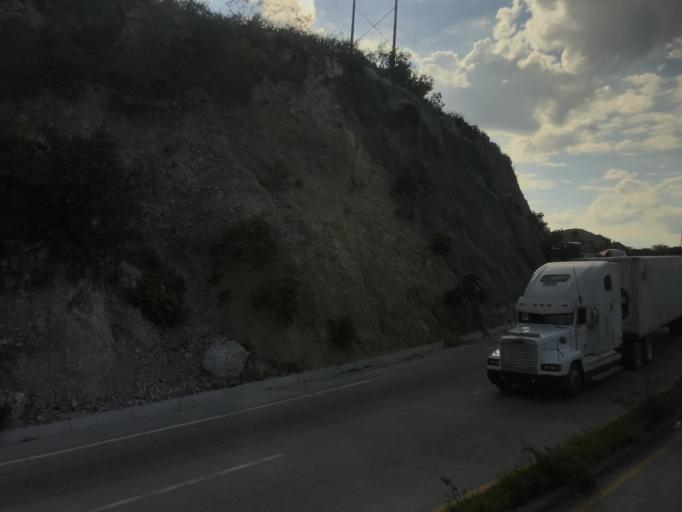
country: GT
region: El Progreso
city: Guastatoya
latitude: 14.8515
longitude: -90.1060
